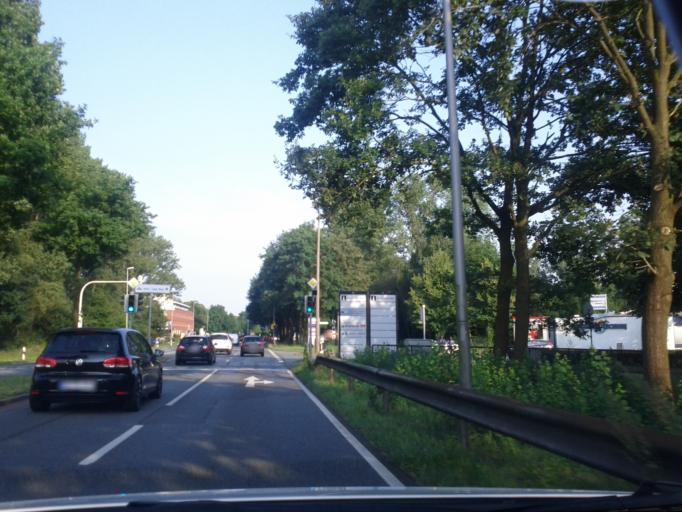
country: DE
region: Lower Saxony
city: Lilienthal
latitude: 53.1108
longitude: 8.8827
